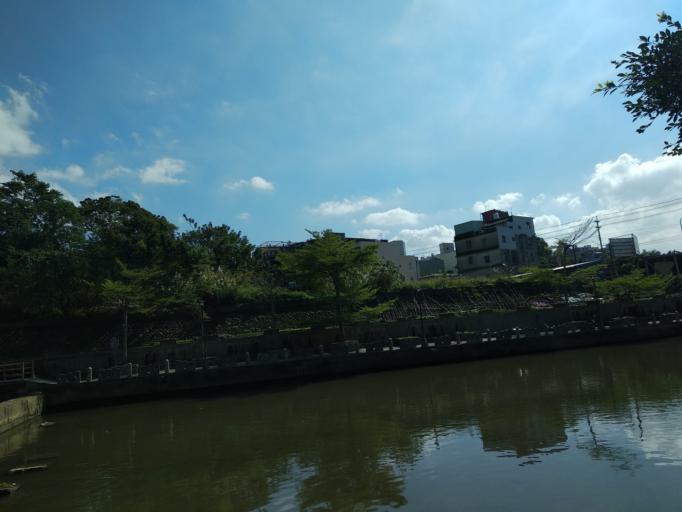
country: TW
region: Taiwan
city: Daxi
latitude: 24.7917
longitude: 121.1803
